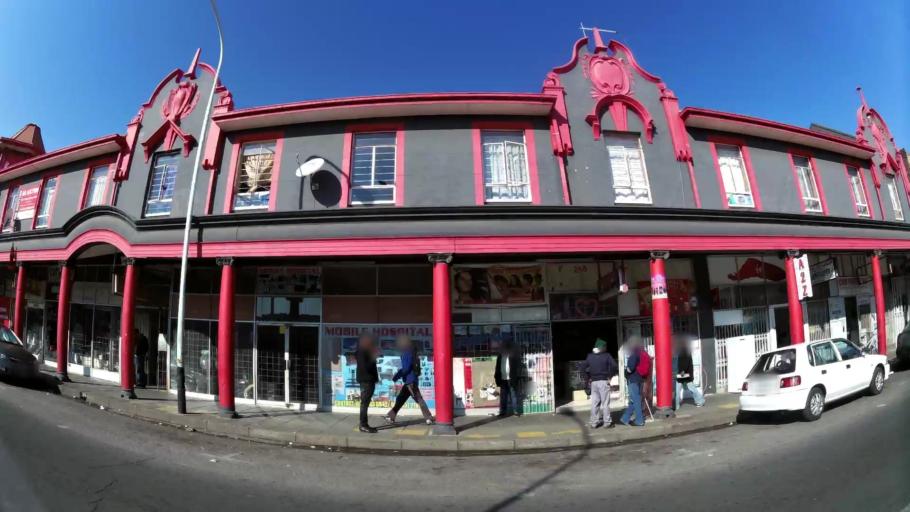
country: ZA
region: Gauteng
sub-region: Ekurhuleni Metropolitan Municipality
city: Boksburg
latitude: -26.2231
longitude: 28.2505
